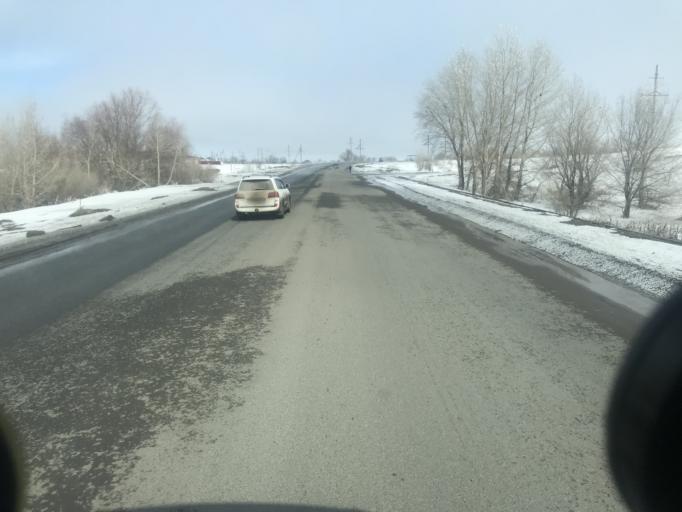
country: KZ
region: Aqtoebe
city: Aqtobe
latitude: 50.2855
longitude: 57.2849
